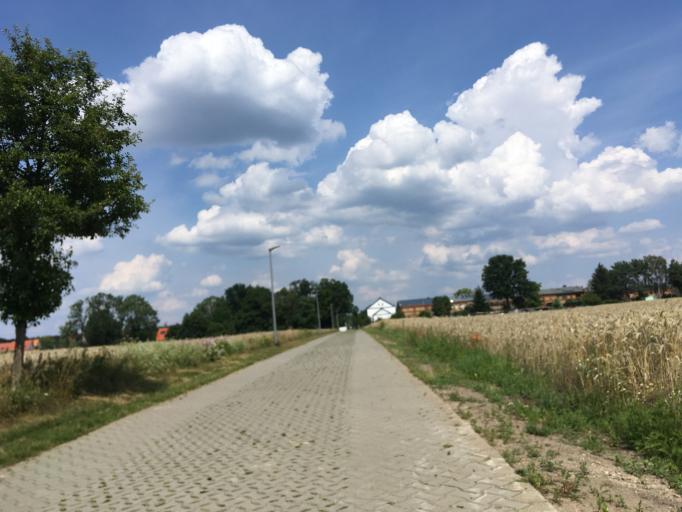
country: DE
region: Berlin
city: Blankenfelde
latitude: 52.6697
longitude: 13.3729
